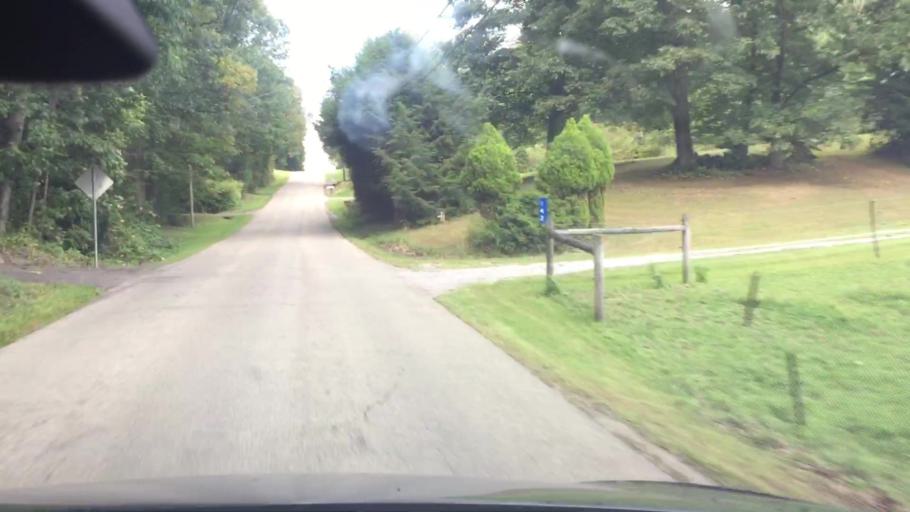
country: US
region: Pennsylvania
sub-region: Butler County
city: Nixon
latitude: 40.7639
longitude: -79.8854
